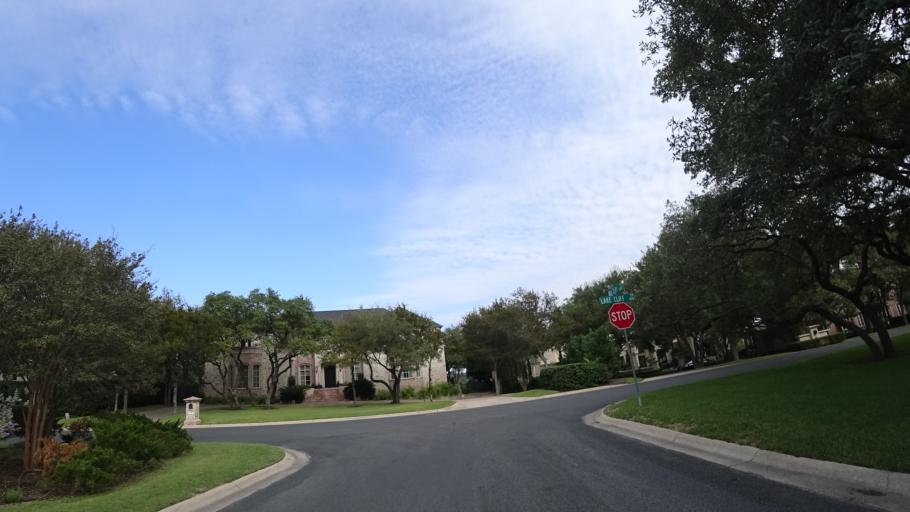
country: US
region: Texas
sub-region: Travis County
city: Rollingwood
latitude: 30.2888
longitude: -97.7886
